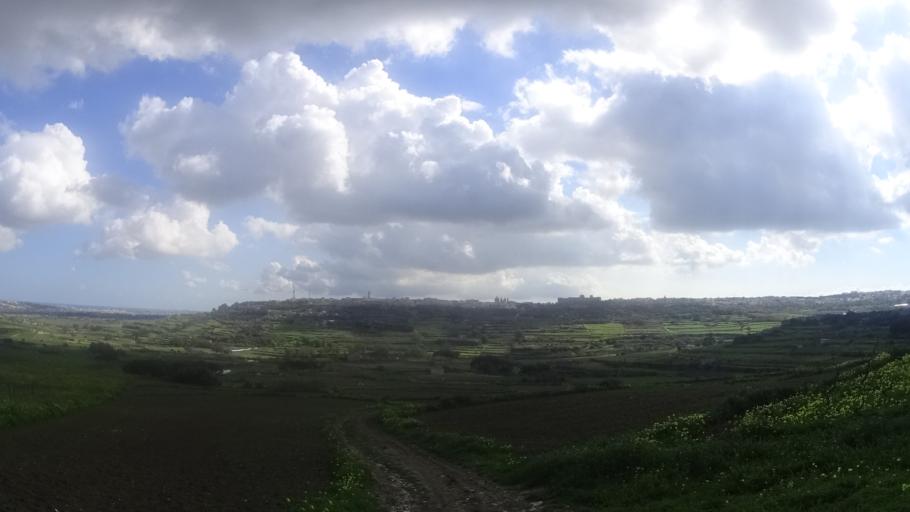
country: MT
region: L-Imtarfa
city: Imtarfa
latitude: 35.8990
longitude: 14.3862
